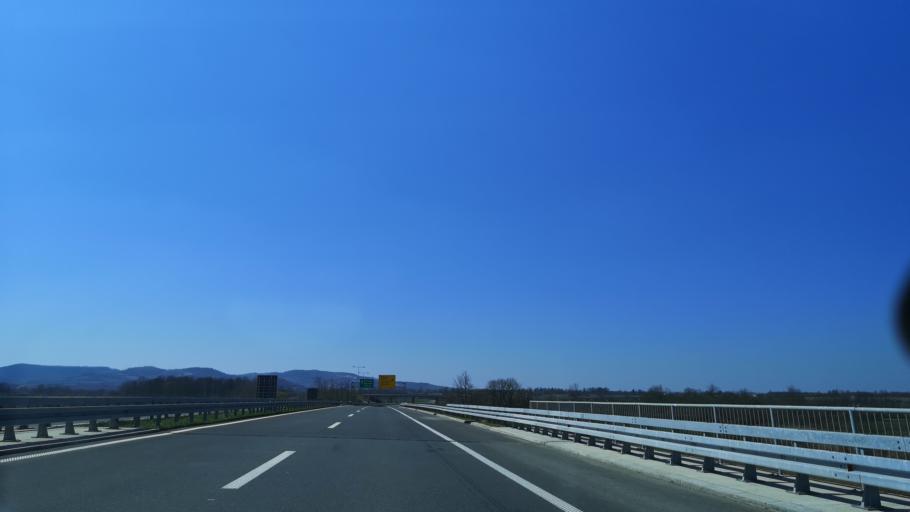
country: RS
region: Central Serbia
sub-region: Kolubarski Okrug
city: Lajkovac
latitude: 44.3557
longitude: 20.1362
